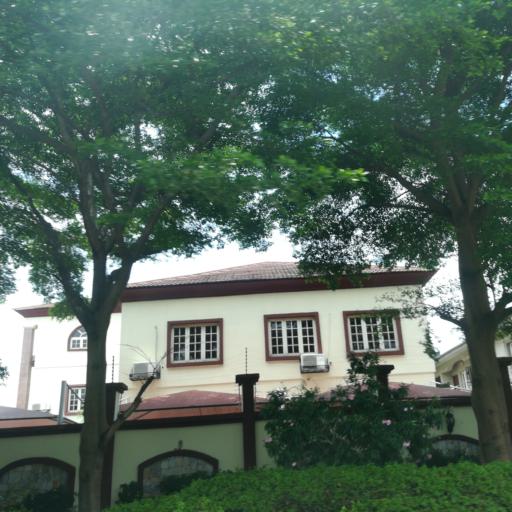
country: NG
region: Lagos
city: Ikoyi
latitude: 6.4441
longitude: 3.4625
